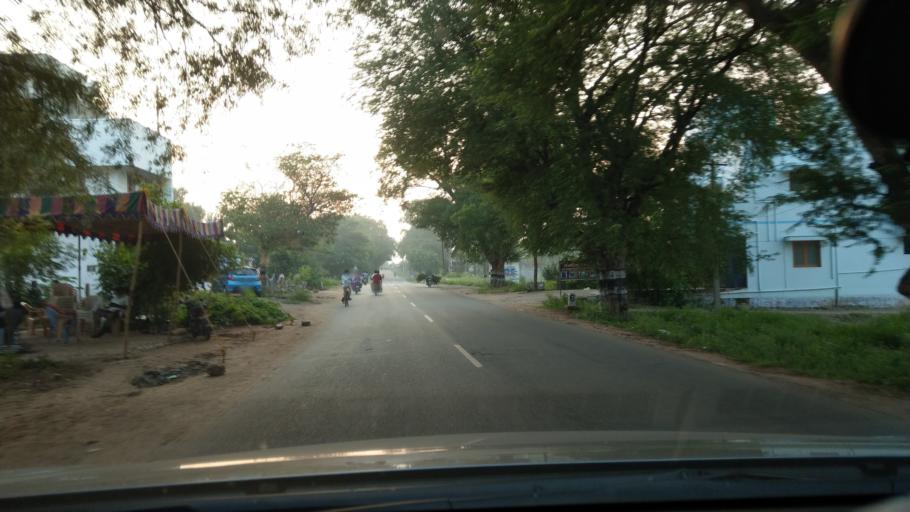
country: IN
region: Tamil Nadu
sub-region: Salem
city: Attur
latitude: 11.5992
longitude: 78.5784
